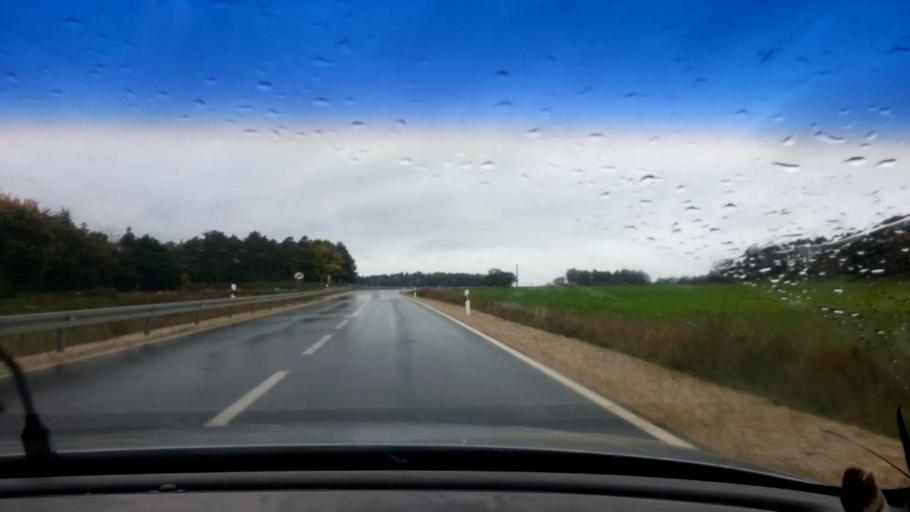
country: DE
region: Bavaria
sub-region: Upper Franconia
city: Poxdorf
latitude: 49.9272
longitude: 11.0844
